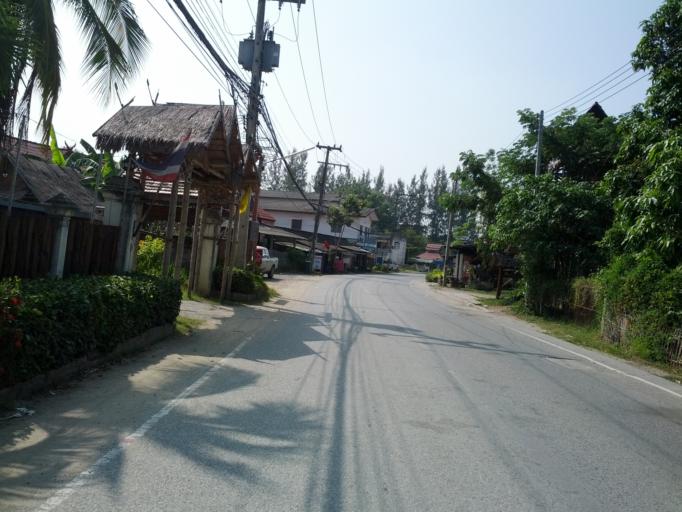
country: TH
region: Chiang Mai
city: San Kamphaeng
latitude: 18.7705
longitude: 99.0752
